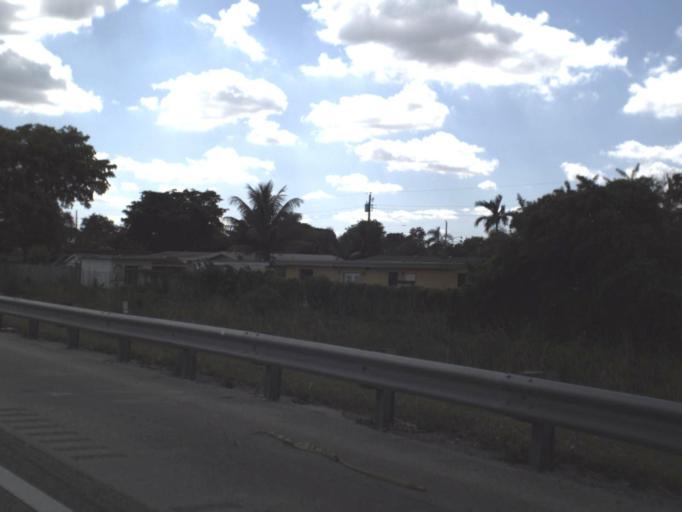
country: US
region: Florida
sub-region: Broward County
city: Miramar
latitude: 25.9855
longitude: -80.2297
